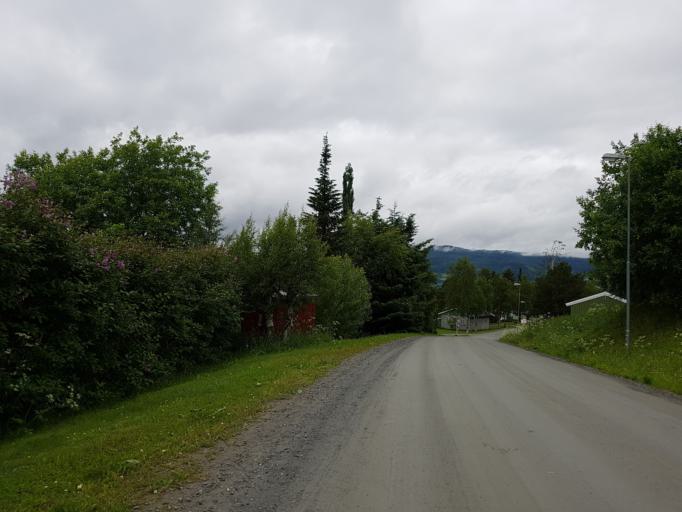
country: NO
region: Sor-Trondelag
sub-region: Selbu
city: Mebonden
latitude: 63.2249
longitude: 11.0306
